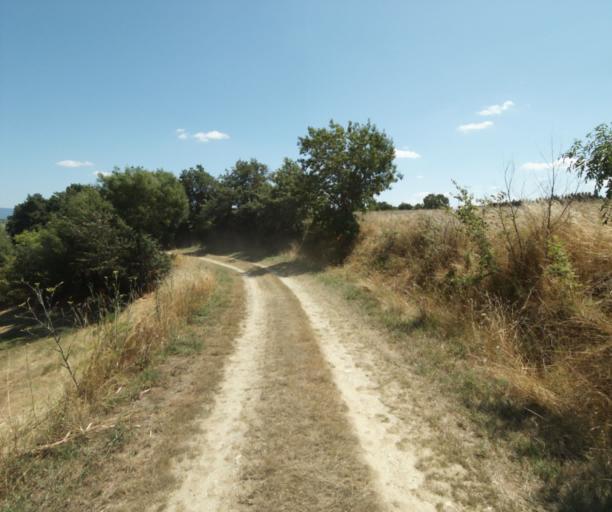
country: FR
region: Midi-Pyrenees
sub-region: Departement de la Haute-Garonne
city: Saint-Felix-Lauragais
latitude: 43.4854
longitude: 1.8659
